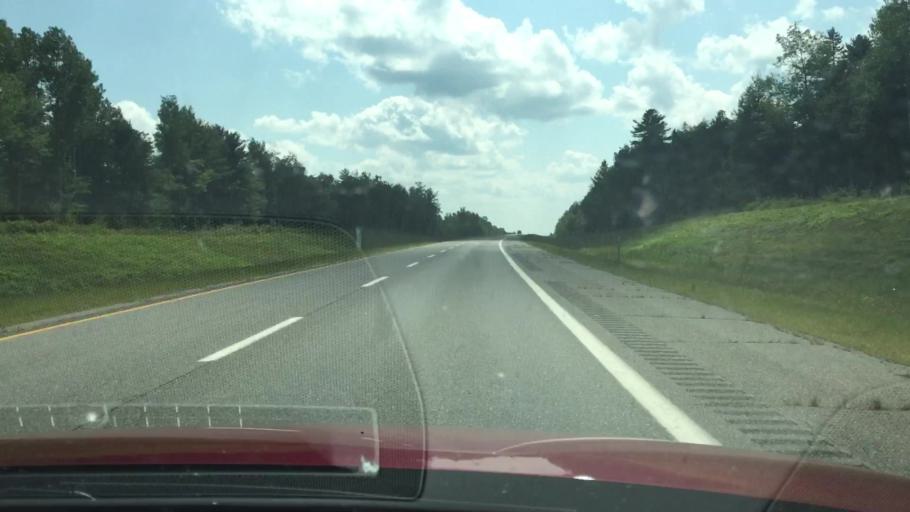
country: US
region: Maine
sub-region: Penobscot County
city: Lincoln
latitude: 45.4232
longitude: -68.5904
